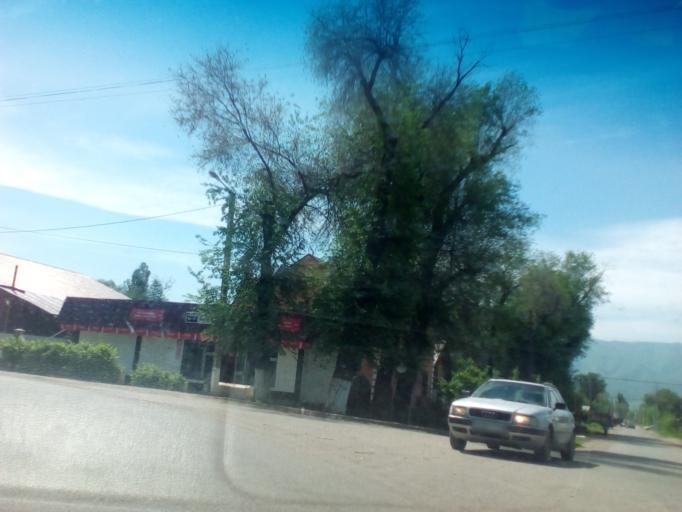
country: KZ
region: Almaty Oblysy
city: Burunday
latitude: 43.2115
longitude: 76.3152
